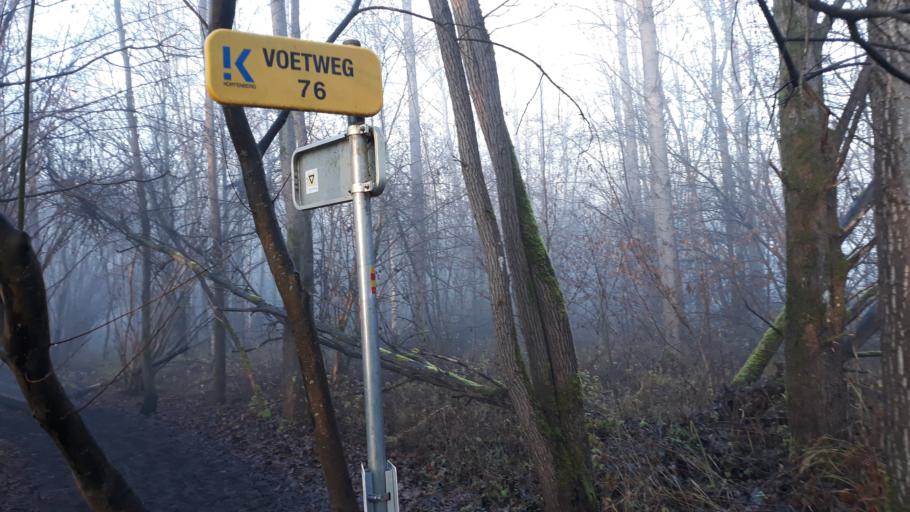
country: BE
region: Flanders
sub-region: Provincie Vlaams-Brabant
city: Kampenhout
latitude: 50.9121
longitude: 4.5783
